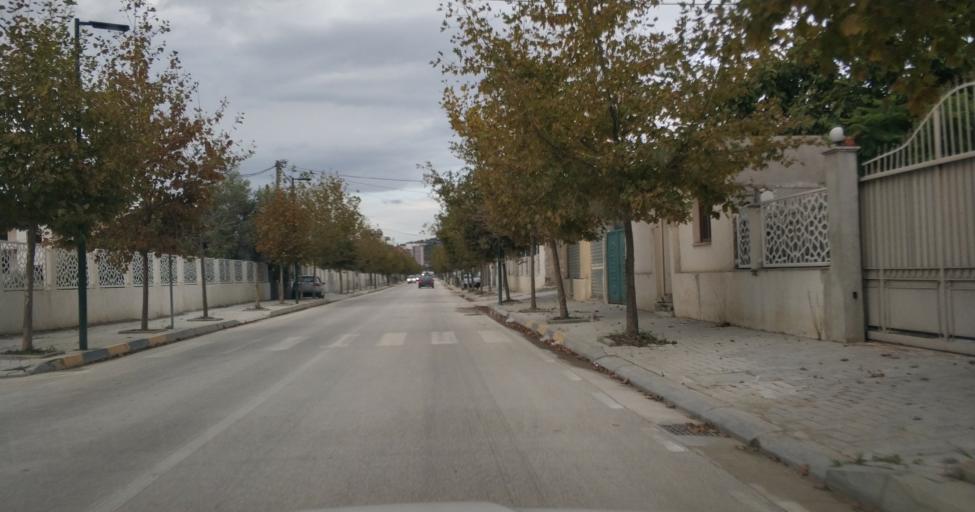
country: AL
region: Vlore
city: Vlore
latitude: 40.4494
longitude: 19.4970
